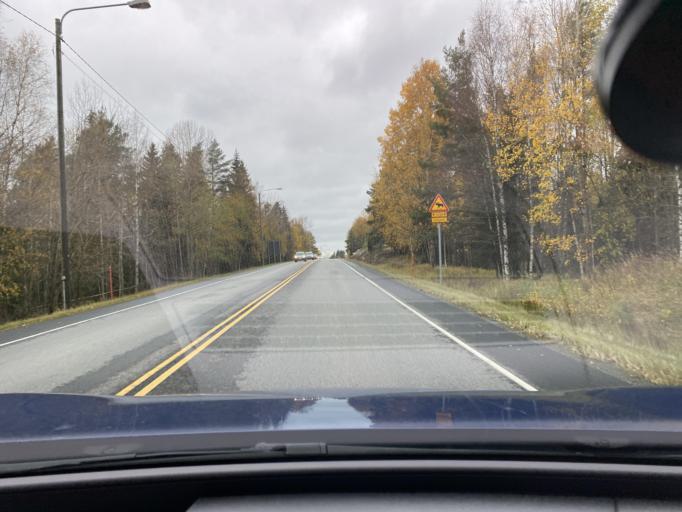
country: FI
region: Satakunta
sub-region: Rauma
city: Rauma
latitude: 61.1257
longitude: 21.6135
